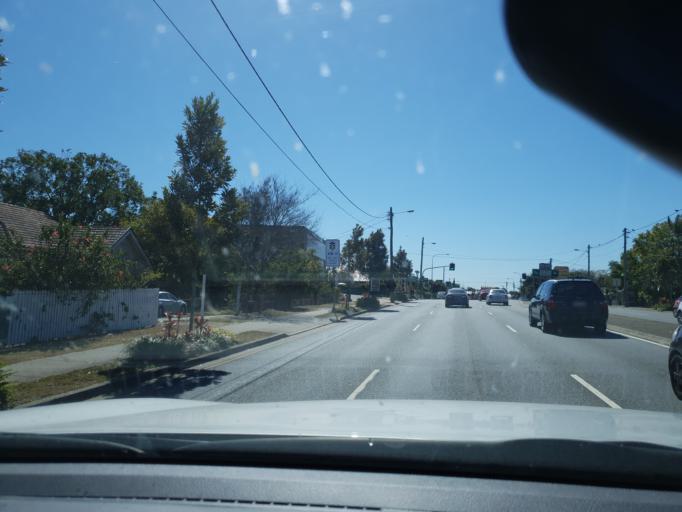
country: AU
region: Queensland
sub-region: Brisbane
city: Annerley
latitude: -27.5149
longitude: 153.0304
